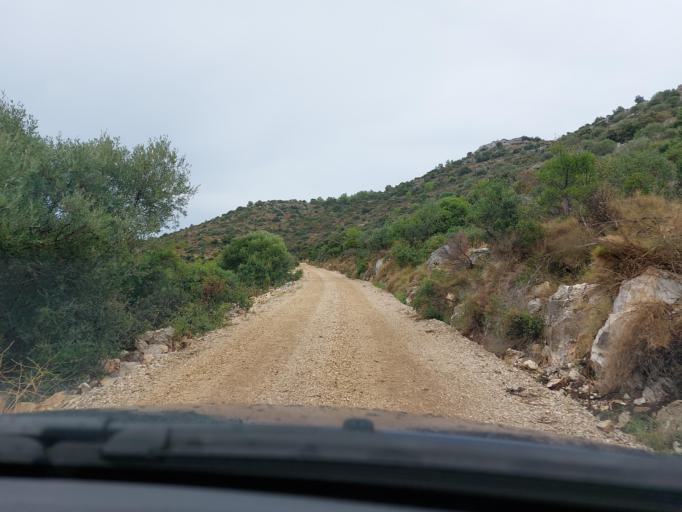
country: HR
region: Dubrovacko-Neretvanska
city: Smokvica
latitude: 42.7395
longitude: 16.9113
